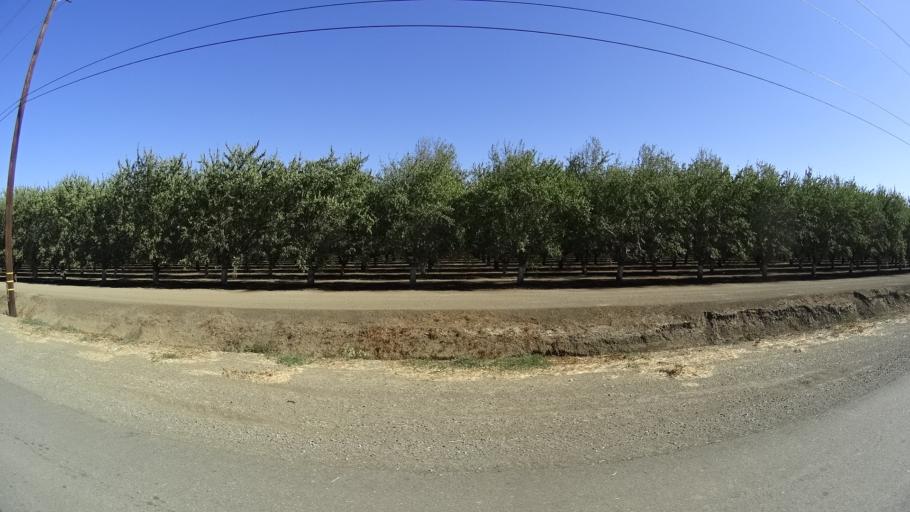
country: US
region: California
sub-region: Yolo County
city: Davis
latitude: 38.5996
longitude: -121.8030
